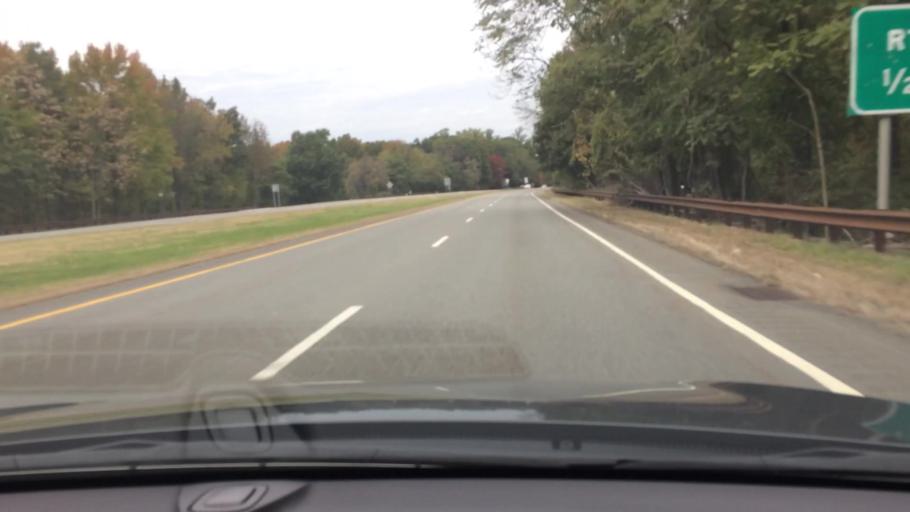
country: US
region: New York
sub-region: Westchester County
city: Hastings-on-Hudson
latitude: 40.9910
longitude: -73.9129
